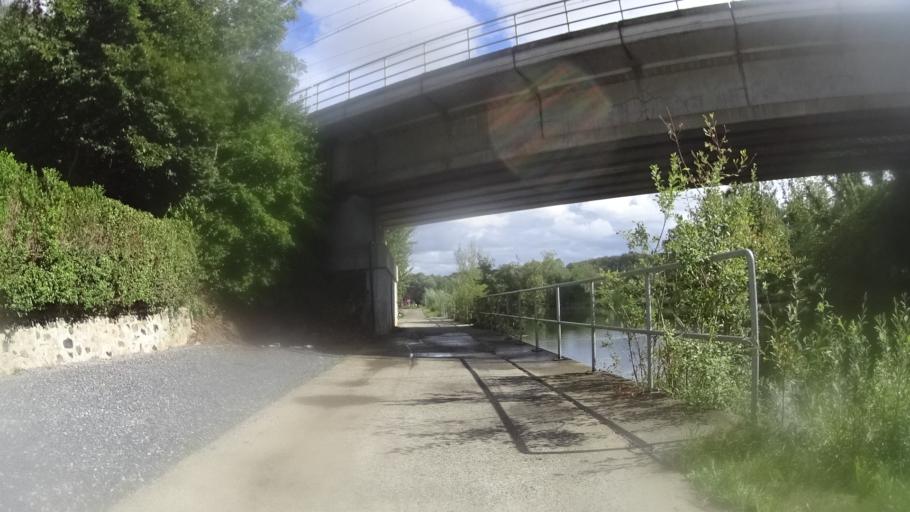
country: BE
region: Wallonia
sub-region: Province du Hainaut
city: Merbes-le-Chateau
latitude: 50.3160
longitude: 4.1827
